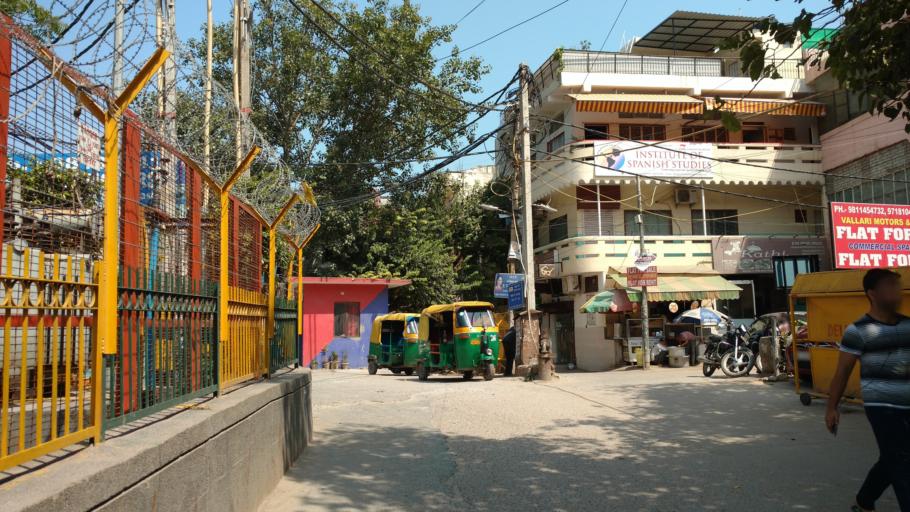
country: IN
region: NCT
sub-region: New Delhi
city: New Delhi
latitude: 28.5306
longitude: 77.2188
